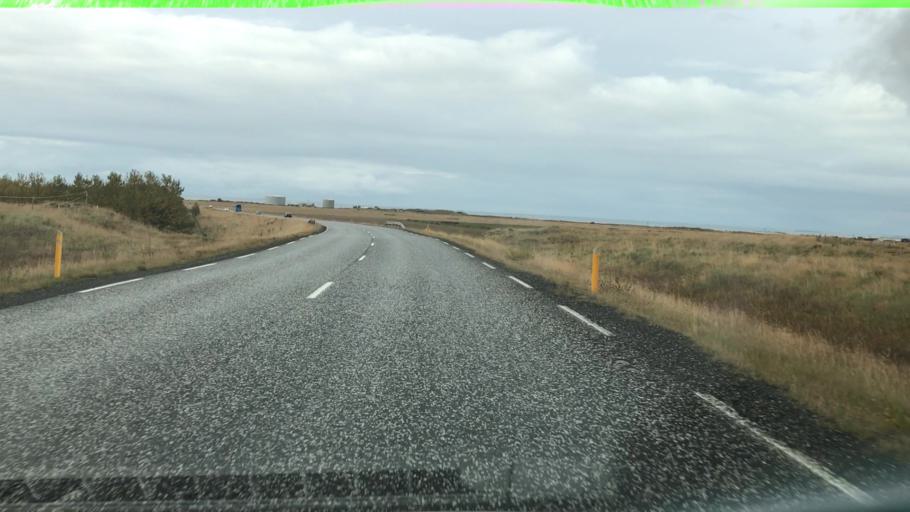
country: IS
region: West
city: Akranes
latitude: 64.3246
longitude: -22.0162
